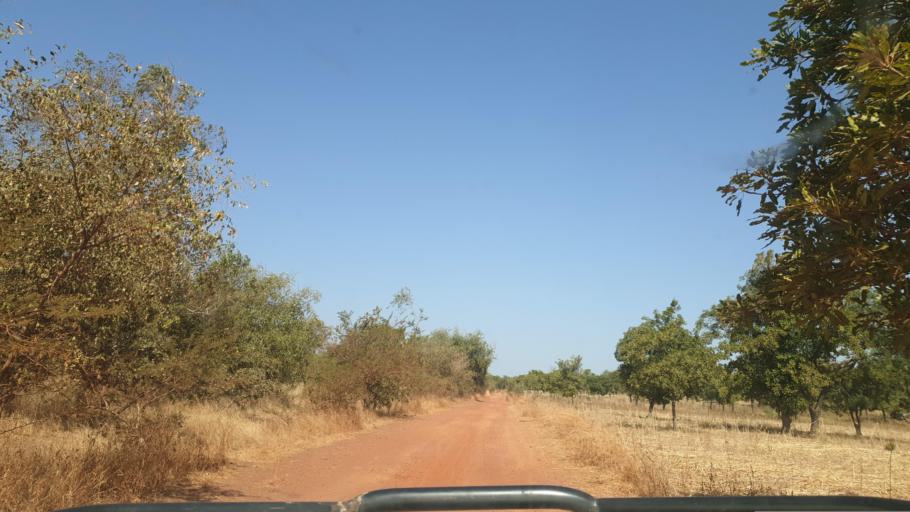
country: ML
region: Koulikoro
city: Dioila
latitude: 11.9058
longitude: -6.9829
